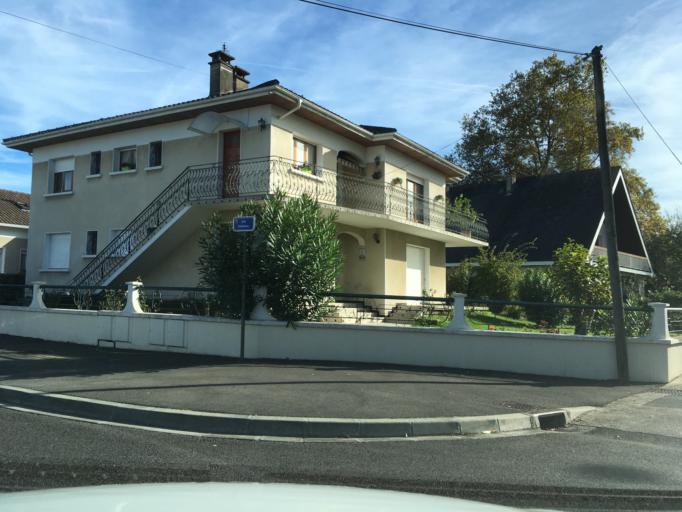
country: FR
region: Aquitaine
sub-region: Departement des Pyrenees-Atlantiques
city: Pau
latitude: 43.3271
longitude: -0.3681
